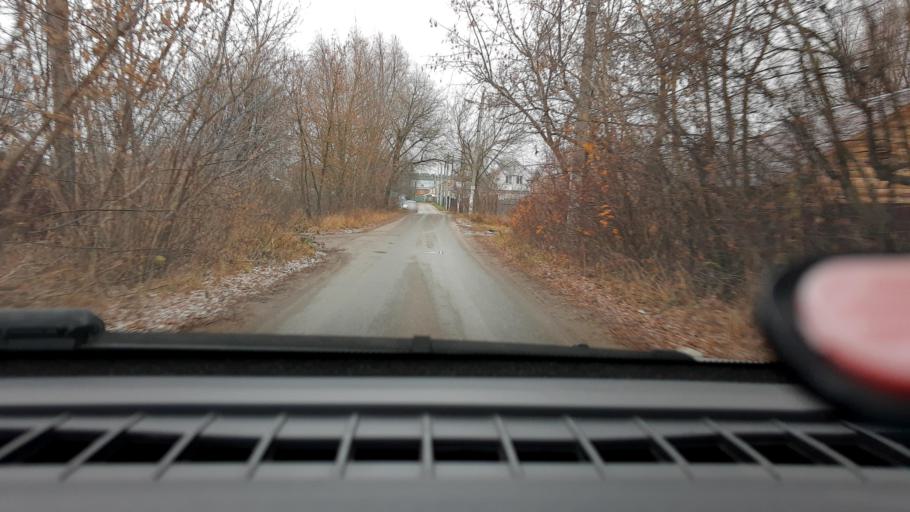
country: RU
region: Nizjnij Novgorod
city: Burevestnik
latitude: 56.2054
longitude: 43.7981
